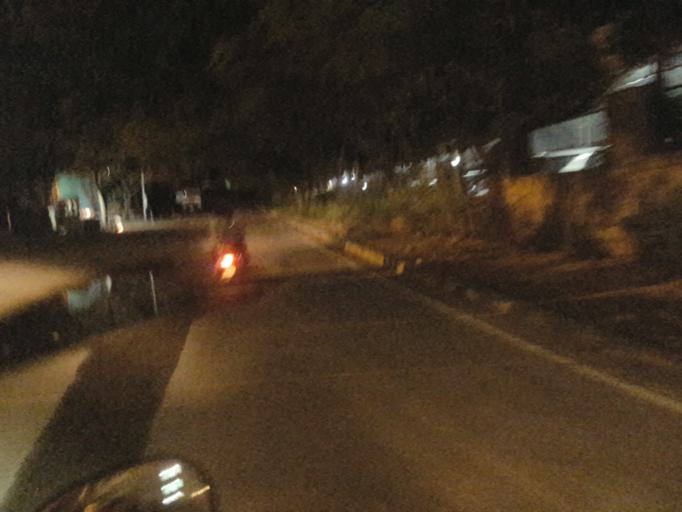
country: IN
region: Telangana
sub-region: Rangareddi
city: Kukatpalli
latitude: 17.4758
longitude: 78.3918
